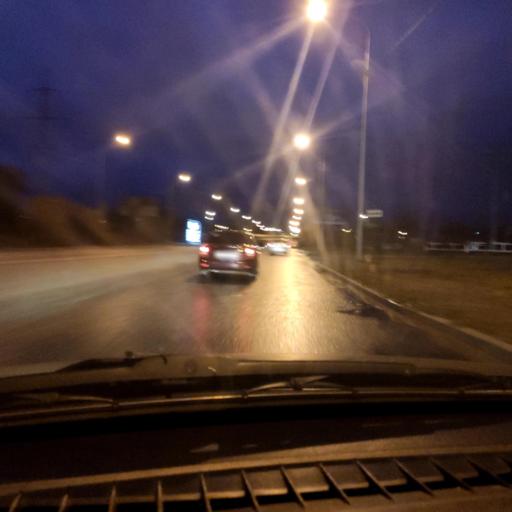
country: RU
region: Samara
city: Tol'yatti
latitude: 53.5696
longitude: 49.2915
